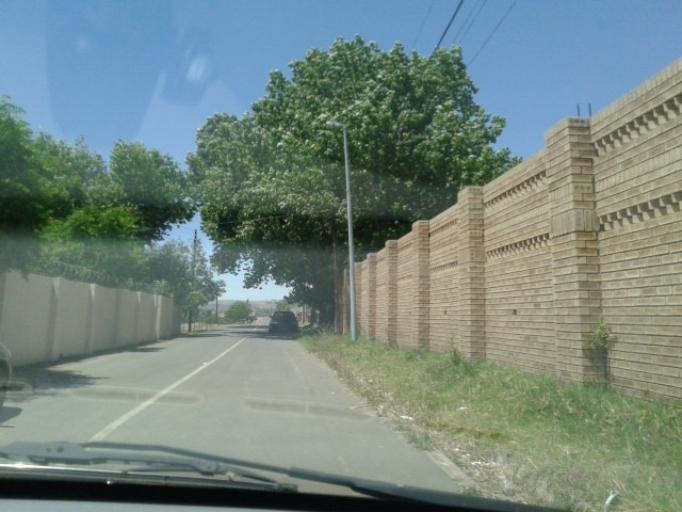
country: LS
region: Maseru
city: Maseru
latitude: -29.3018
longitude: 27.4763
